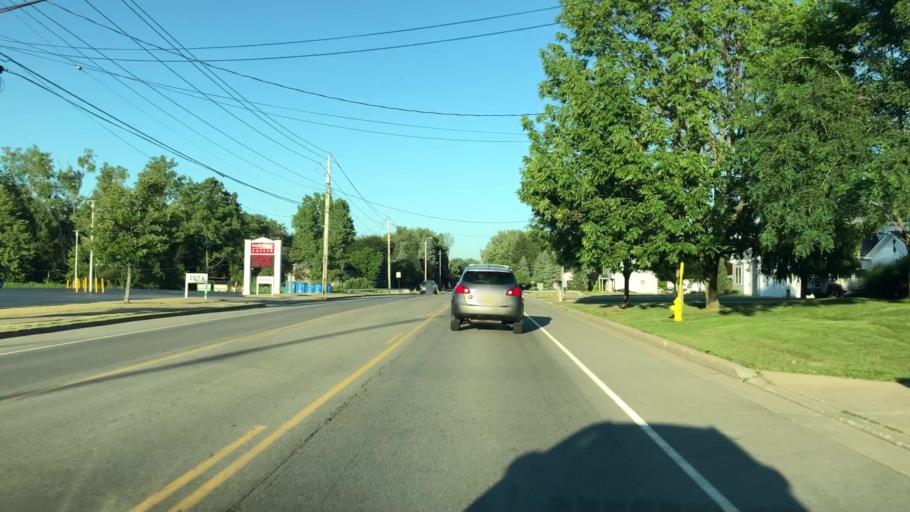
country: US
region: New York
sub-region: Erie County
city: Cheektowaga
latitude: 42.8806
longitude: -78.7254
